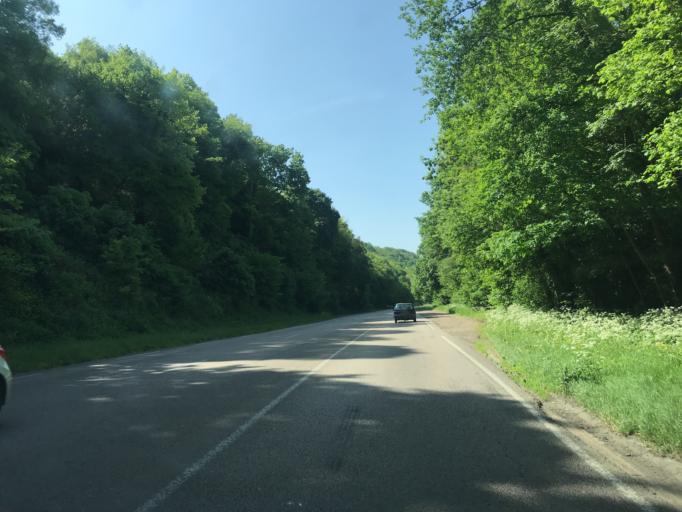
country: FR
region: Haute-Normandie
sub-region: Departement de la Seine-Maritime
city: Les Authieux-sur-le-Port-Saint-Ouen
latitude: 49.3473
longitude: 1.1270
